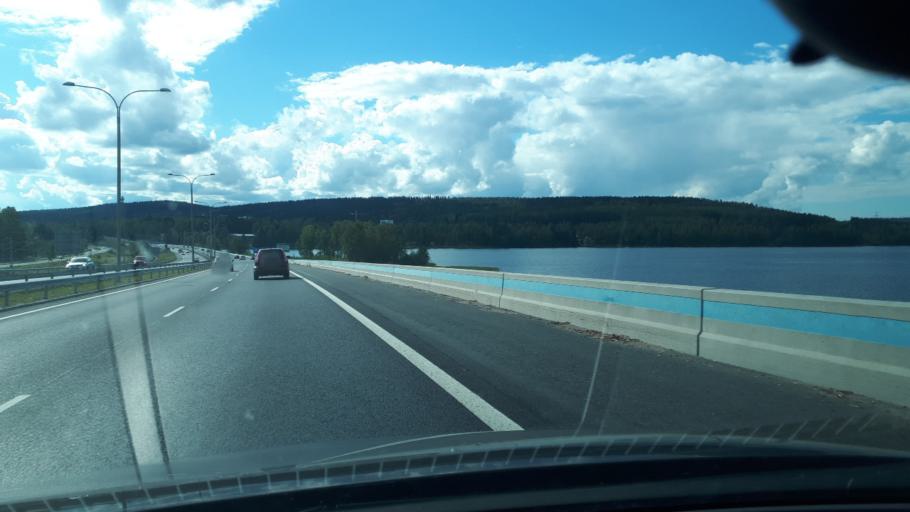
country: FI
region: Northern Savo
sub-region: Kuopio
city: Kuopio
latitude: 62.9459
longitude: 27.6704
